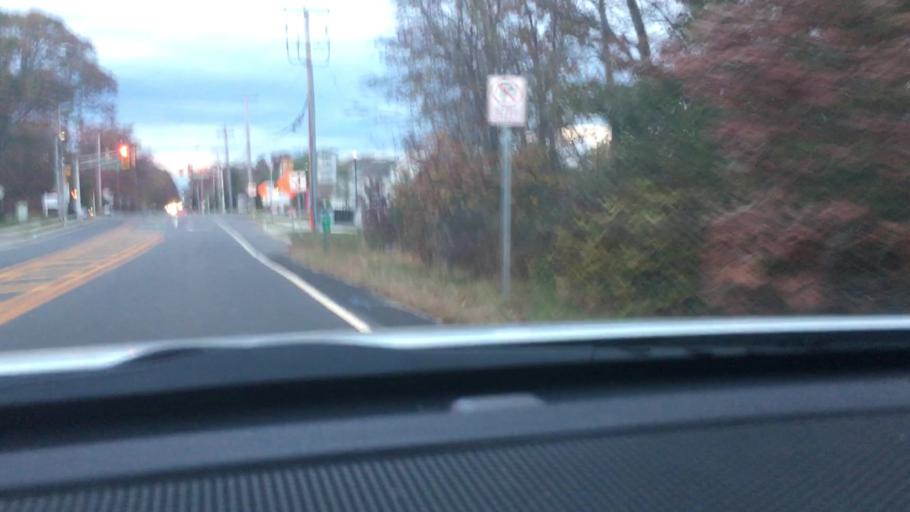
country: US
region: New Jersey
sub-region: Atlantic County
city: Absecon
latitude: 39.4389
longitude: -74.4982
